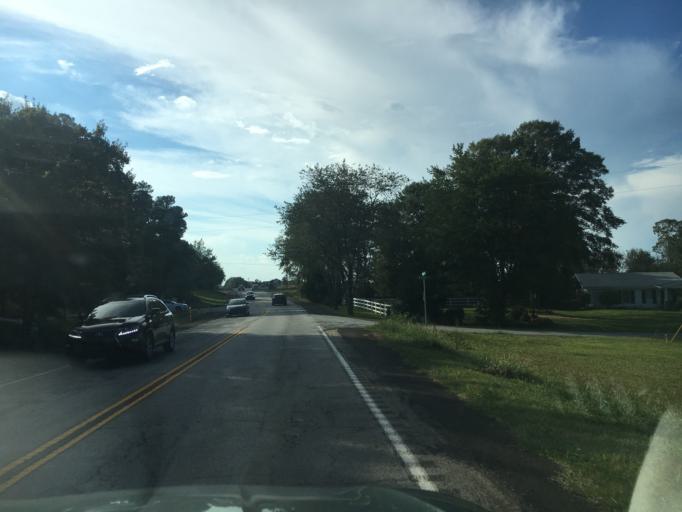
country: US
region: South Carolina
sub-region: Greenville County
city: Five Forks
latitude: 34.7999
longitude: -82.2046
